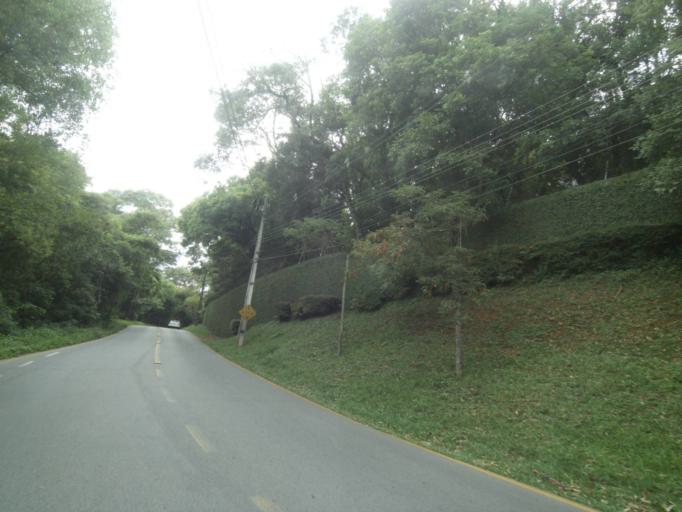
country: BR
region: Parana
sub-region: Curitiba
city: Curitiba
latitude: -25.4043
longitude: -49.3049
